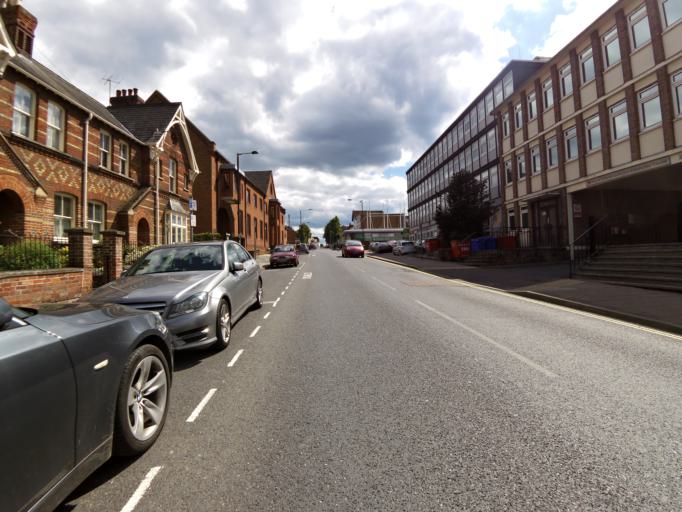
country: GB
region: England
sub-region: Suffolk
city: Bury St Edmunds
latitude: 52.2487
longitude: 0.7113
